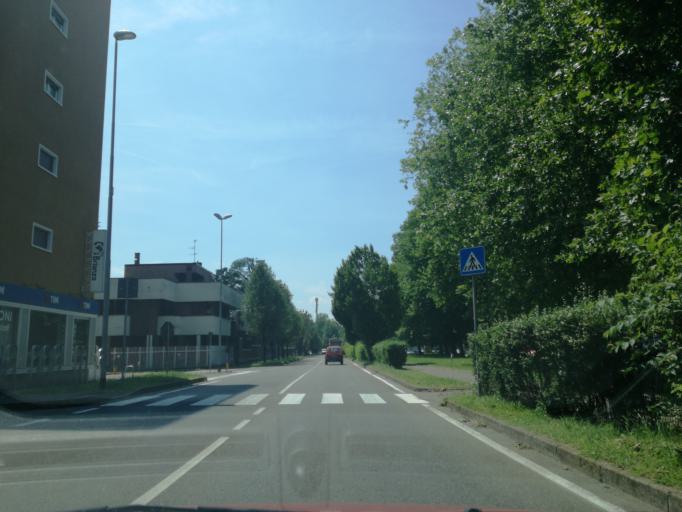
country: IT
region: Lombardy
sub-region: Provincia di Monza e Brianza
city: Desio
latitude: 45.6258
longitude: 9.2043
